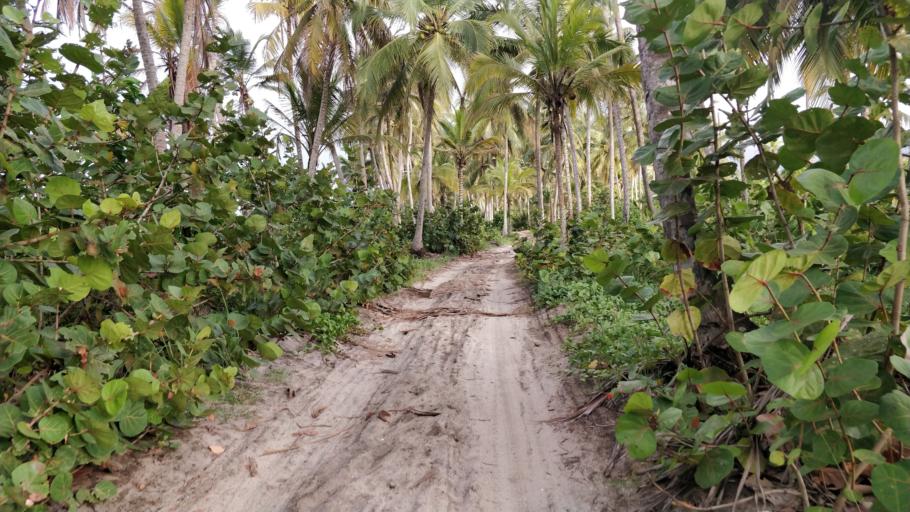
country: CO
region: Magdalena
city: Santa Marta
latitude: 11.2706
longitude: -73.8415
